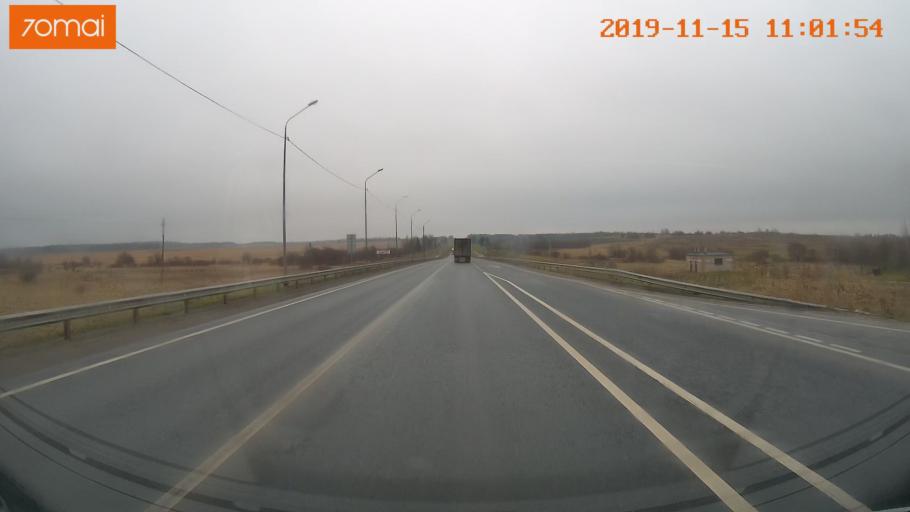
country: RU
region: Vologda
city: Chebsara
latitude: 59.1310
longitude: 38.9298
